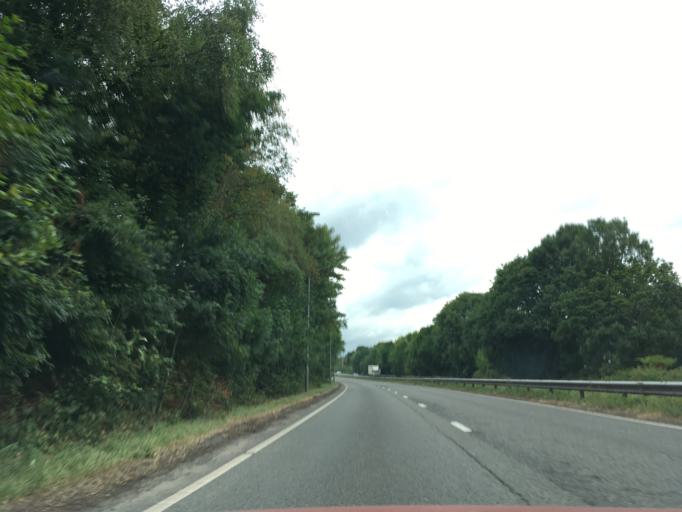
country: GB
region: Wales
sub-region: Torfaen County Borough
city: Cwmbran
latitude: 51.6573
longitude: -2.9989
